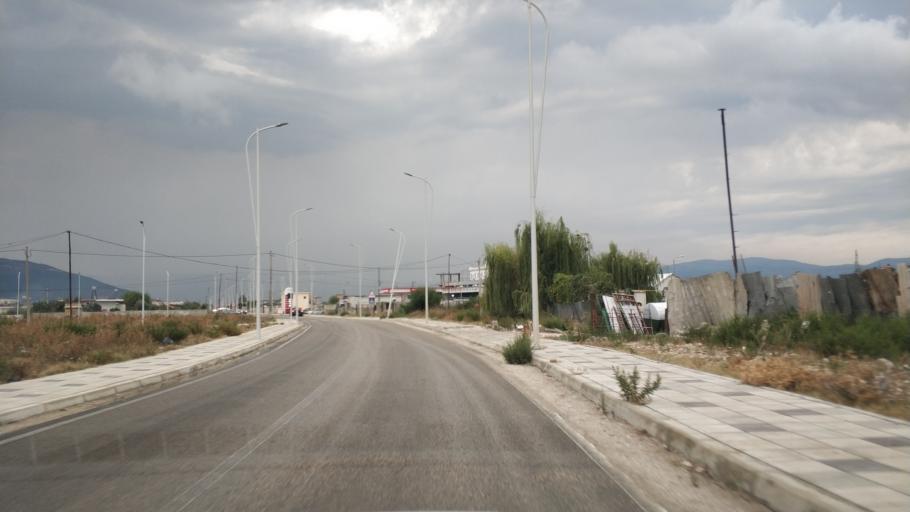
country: AL
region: Vlore
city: Vlore
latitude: 40.4826
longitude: 19.4667
